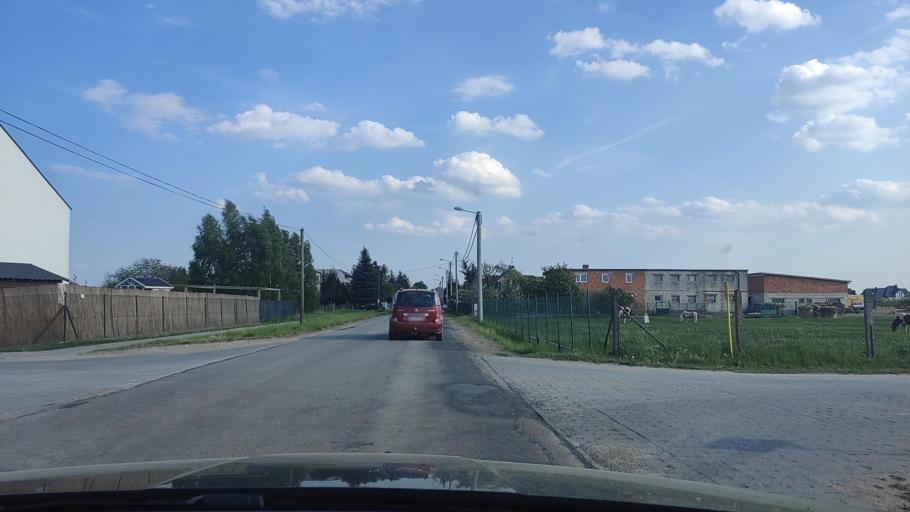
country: PL
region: Greater Poland Voivodeship
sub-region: Powiat poznanski
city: Kleszczewo
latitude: 52.3889
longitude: 17.1587
